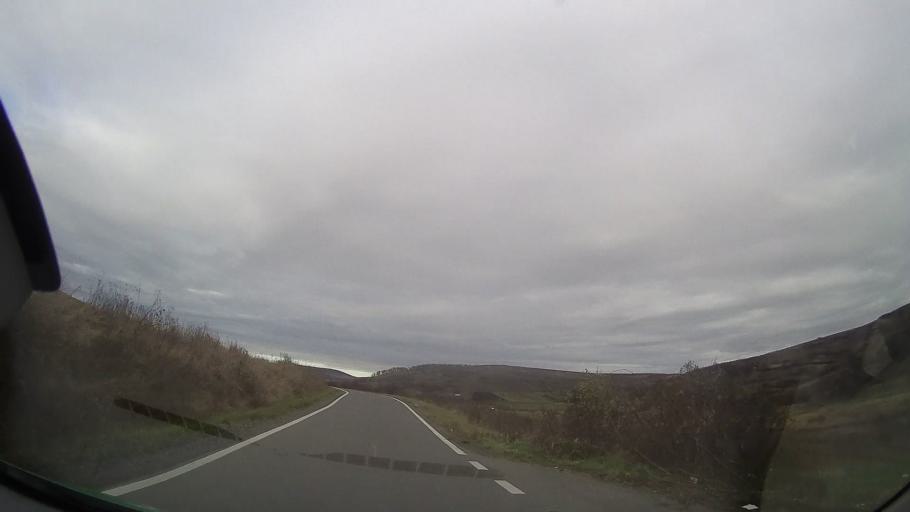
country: RO
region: Mures
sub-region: Comuna Faragau
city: Faragau
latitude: 46.7687
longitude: 24.5578
